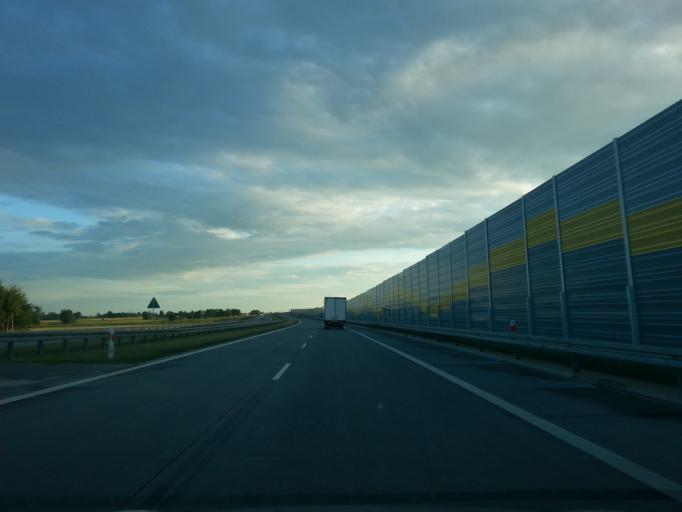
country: PL
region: Lodz Voivodeship
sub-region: Powiat wieruszowski
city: Lututow
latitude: 51.3274
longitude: 18.4434
